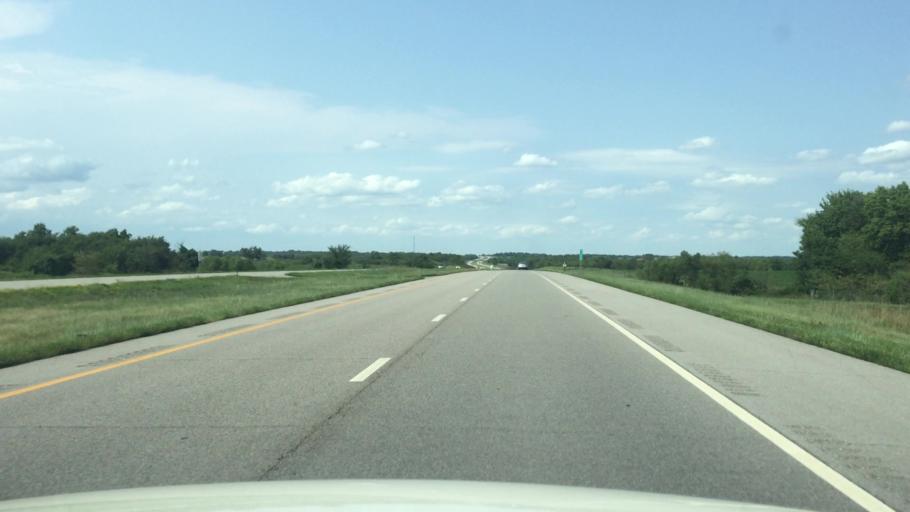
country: US
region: Kansas
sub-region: Linn County
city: La Cygne
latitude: 38.4388
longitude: -94.6865
